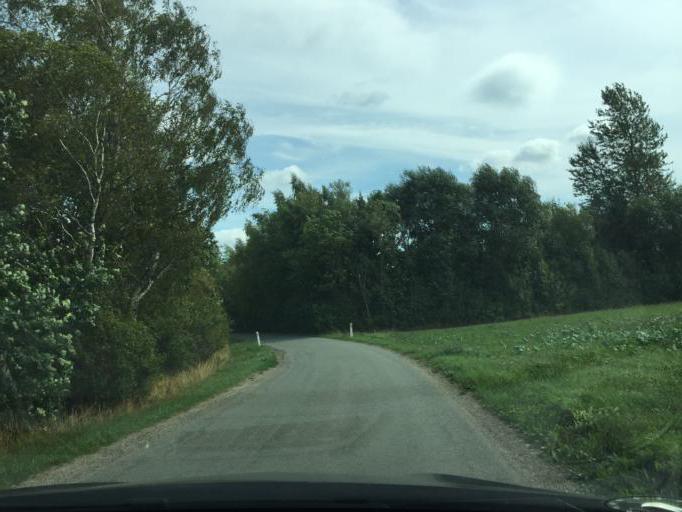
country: DK
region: South Denmark
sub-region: Assens Kommune
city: Tommerup
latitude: 55.3947
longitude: 10.2457
